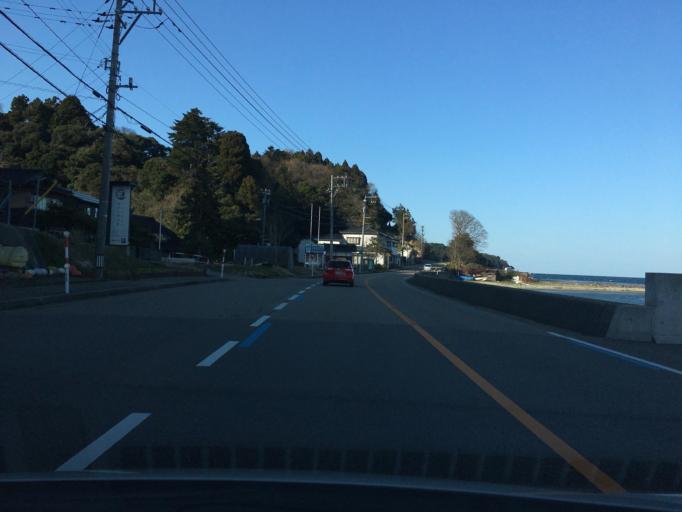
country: JP
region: Toyama
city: Himi
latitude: 36.9028
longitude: 137.0128
